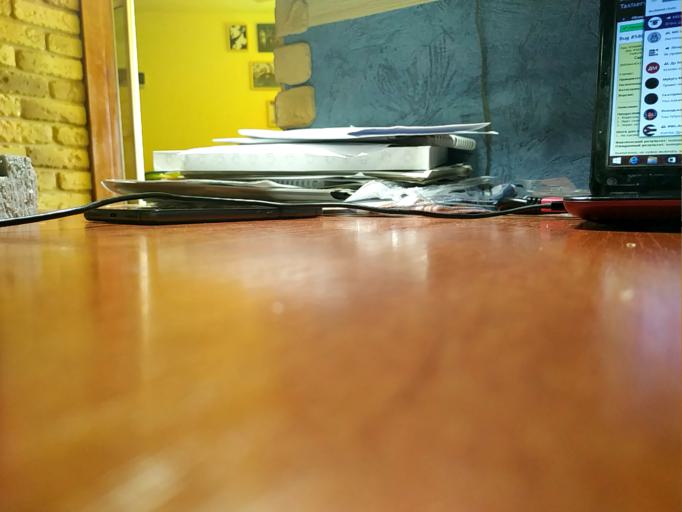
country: RU
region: Vologda
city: Khokhlovo
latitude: 59.4203
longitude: 37.3427
